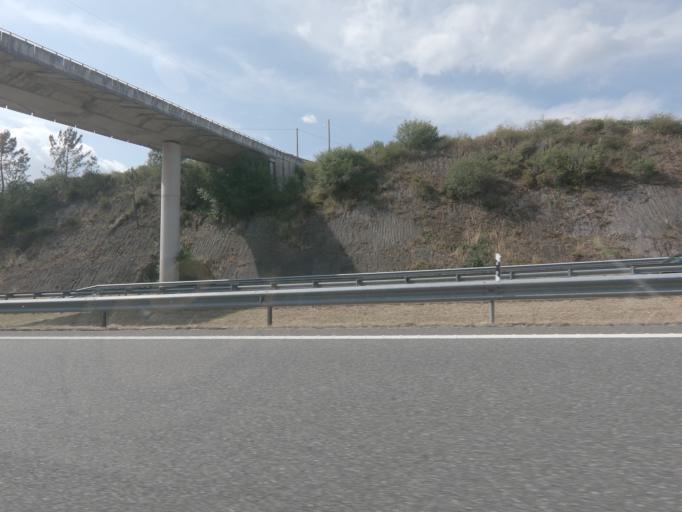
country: ES
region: Galicia
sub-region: Provincia de Ourense
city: Cenlle
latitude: 42.3167
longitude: -8.0866
